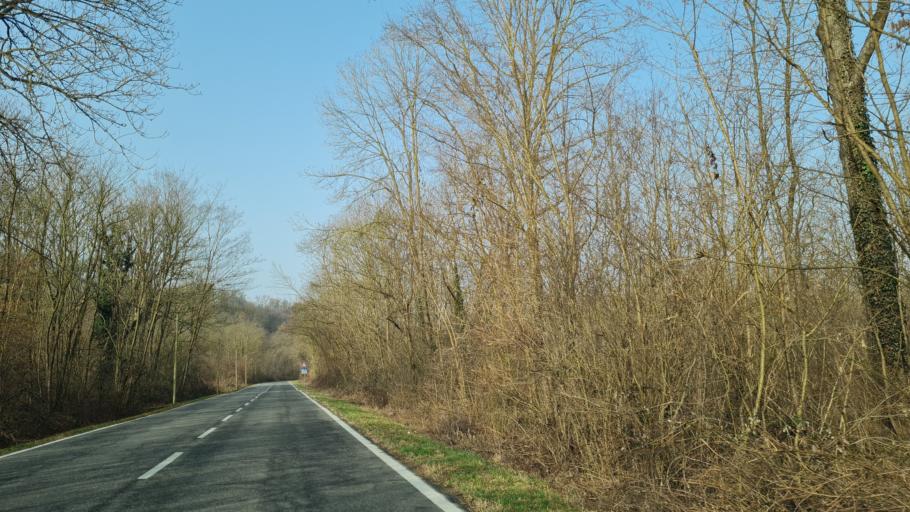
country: IT
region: Piedmont
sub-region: Provincia di Biella
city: Cerrione
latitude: 45.4643
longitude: 8.0656
